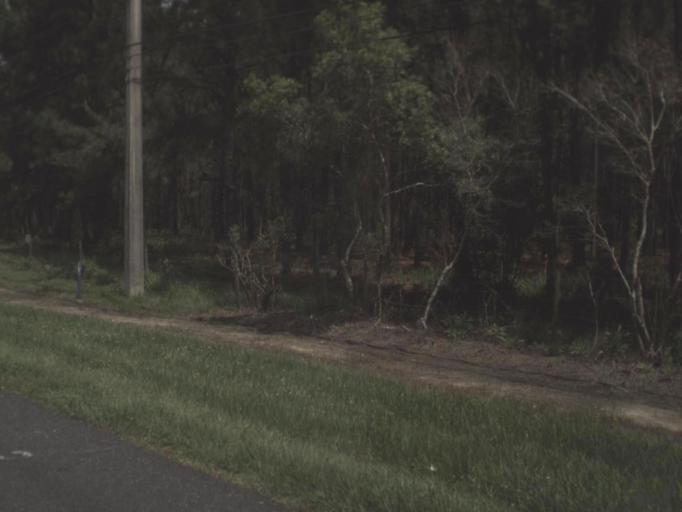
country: US
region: Florida
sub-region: Saint Johns County
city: Fruit Cove
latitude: 30.1482
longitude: -81.5224
